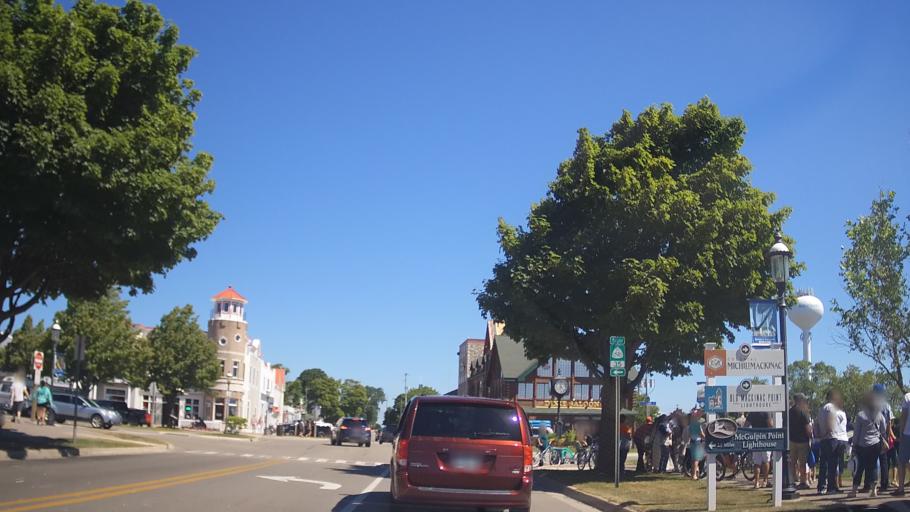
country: US
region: Michigan
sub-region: Mackinac County
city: Saint Ignace
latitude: 45.7810
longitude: -84.7255
